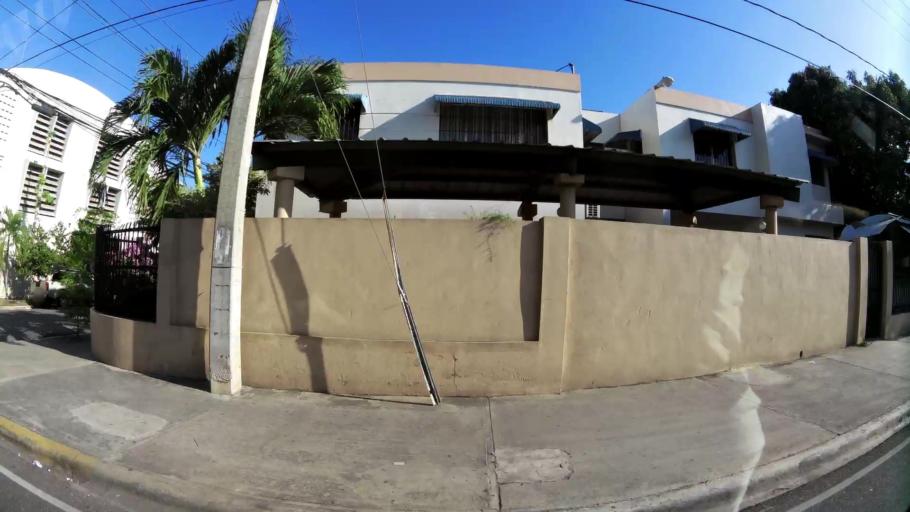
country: DO
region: Nacional
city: La Julia
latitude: 18.4568
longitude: -69.9215
